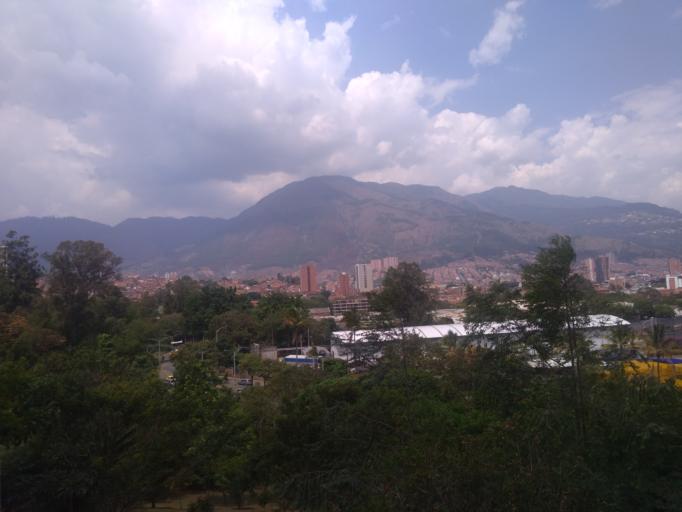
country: CO
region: Antioquia
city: Bello
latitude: 6.3272
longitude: -75.5619
